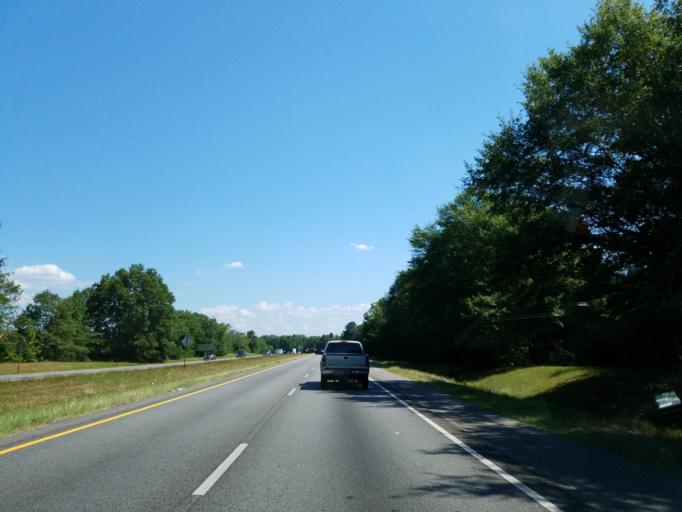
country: US
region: Georgia
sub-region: Spalding County
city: Experiment
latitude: 33.2402
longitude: -84.2957
